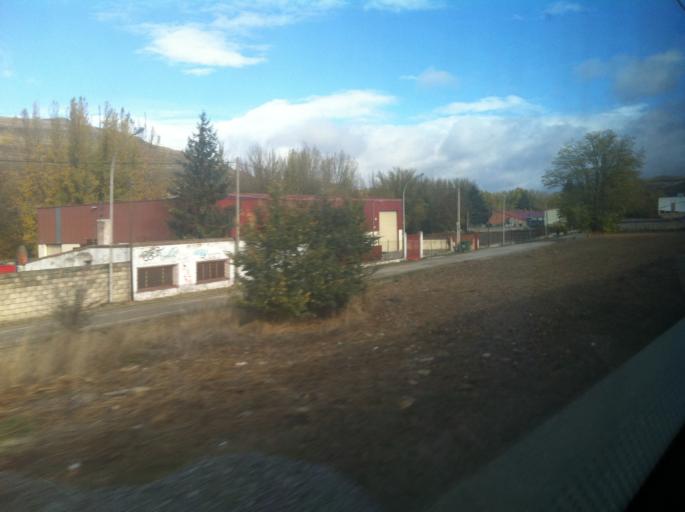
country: ES
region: Castille and Leon
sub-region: Provincia de Burgos
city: Briviesca
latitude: 42.5346
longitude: -3.3228
